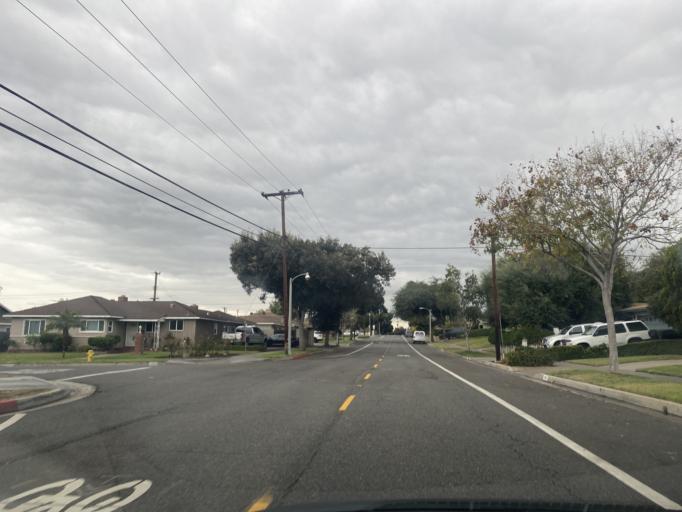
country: US
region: California
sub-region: Orange County
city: Fullerton
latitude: 33.8815
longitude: -117.9014
